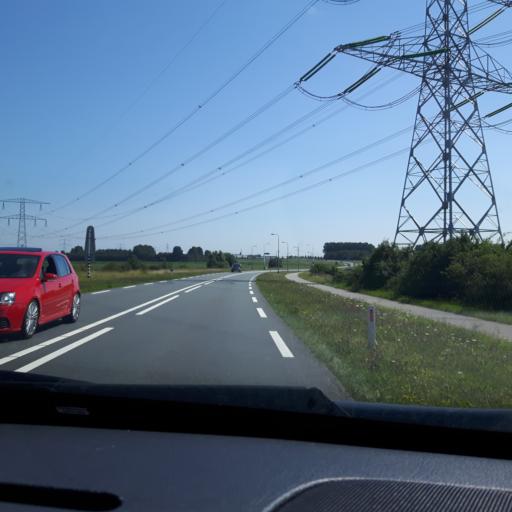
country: NL
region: Zeeland
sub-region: Gemeente Reimerswaal
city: Yerseke
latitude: 51.4686
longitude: 4.0153
